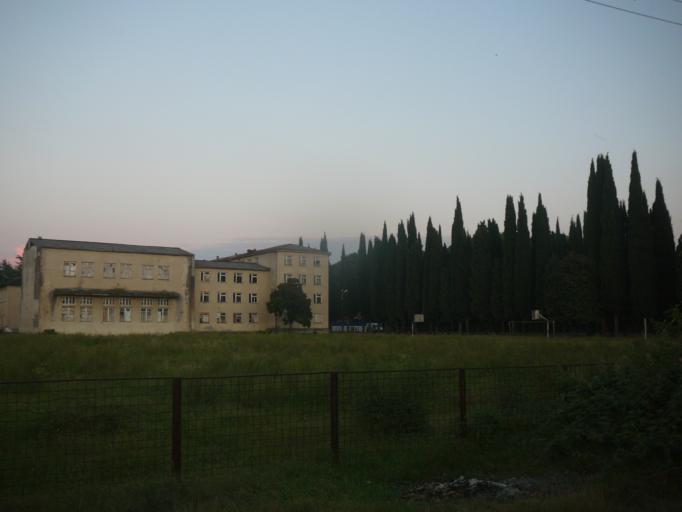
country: GE
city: Gantiadi
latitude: 43.3825
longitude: 40.0434
